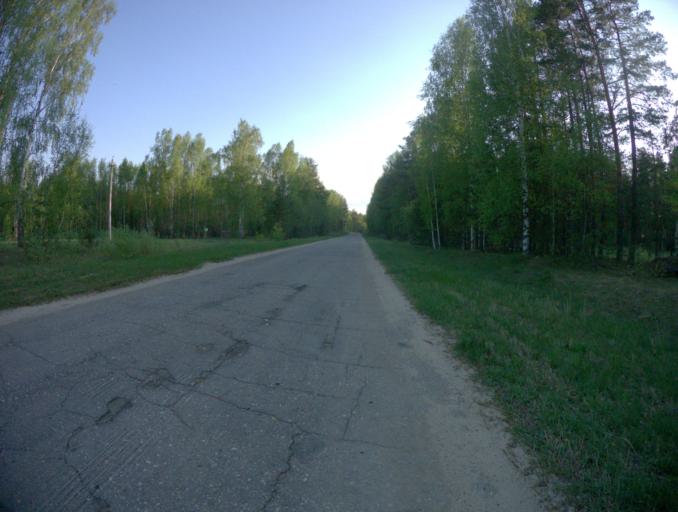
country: RU
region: Vladimir
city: Vyazniki
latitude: 56.3381
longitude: 42.1349
